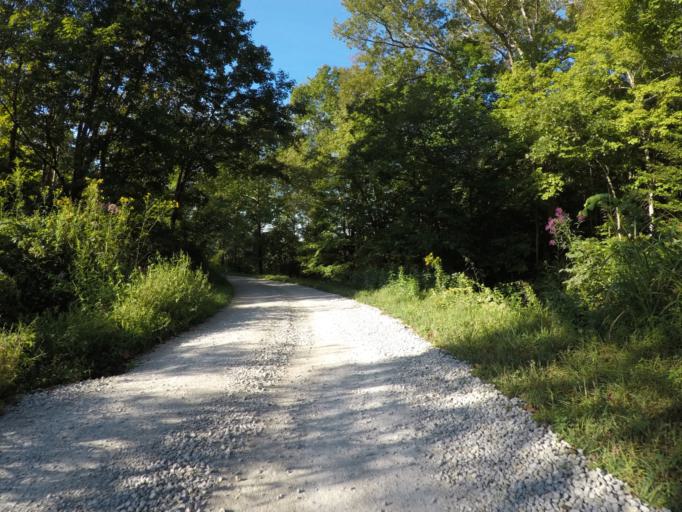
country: US
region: Ohio
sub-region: Lawrence County
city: Coal Grove
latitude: 38.5779
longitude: -82.5449
